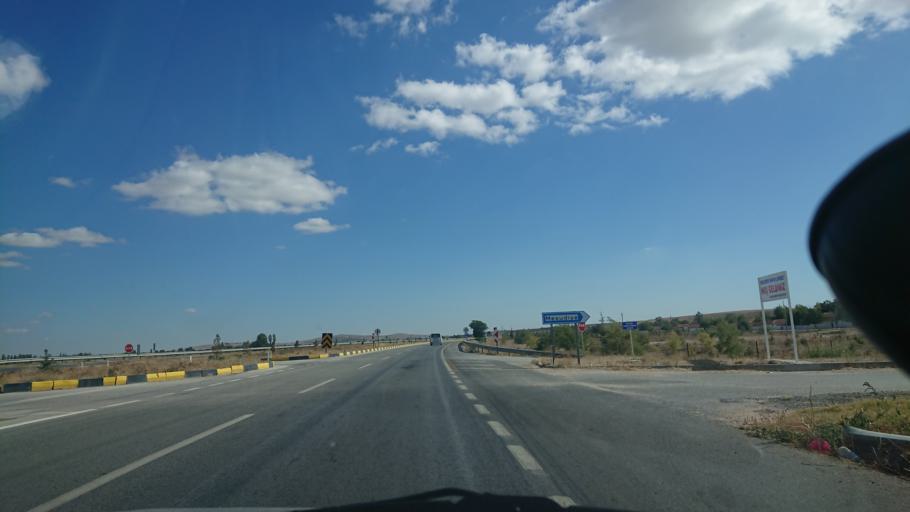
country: TR
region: Eskisehir
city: Mahmudiye
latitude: 39.5386
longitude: 30.9421
